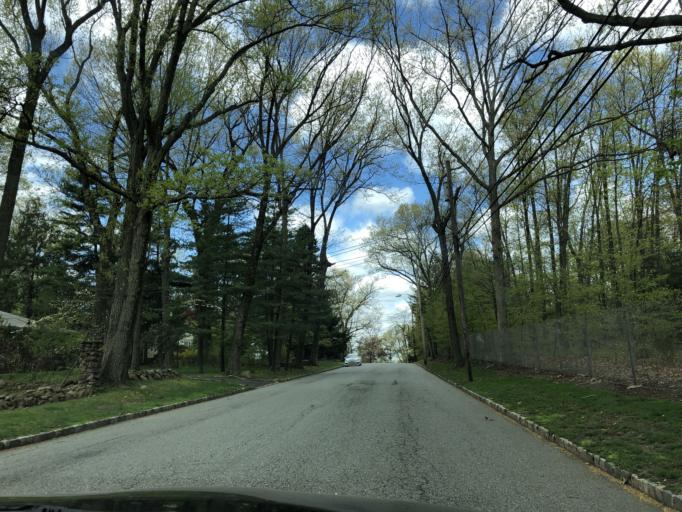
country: US
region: New Jersey
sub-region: Essex County
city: Caldwell
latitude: 40.8327
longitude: -74.2757
